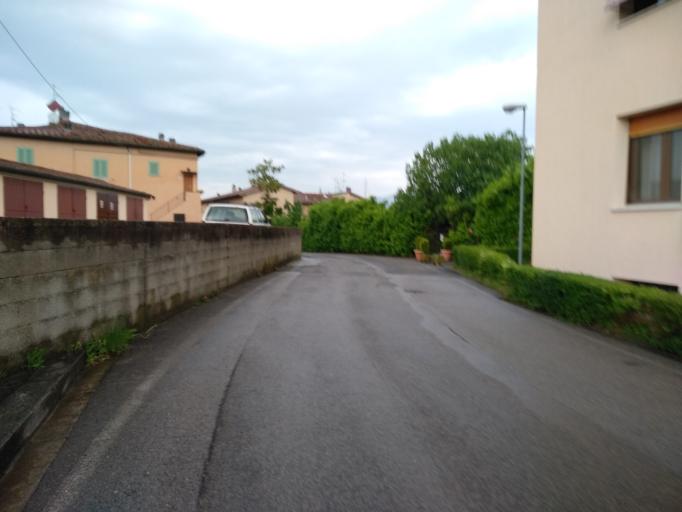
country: IT
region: Tuscany
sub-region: Province of Arezzo
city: San Giovanni Valdarno
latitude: 43.5605
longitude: 11.5290
